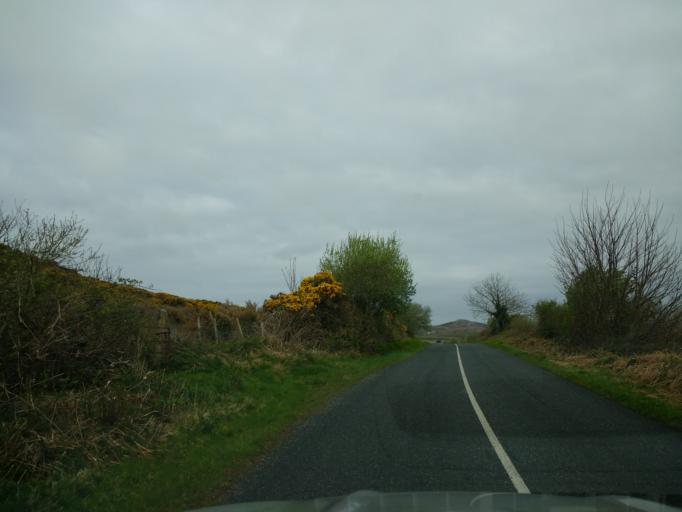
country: IE
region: Ulster
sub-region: County Donegal
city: Buncrana
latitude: 55.1639
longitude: -7.5692
